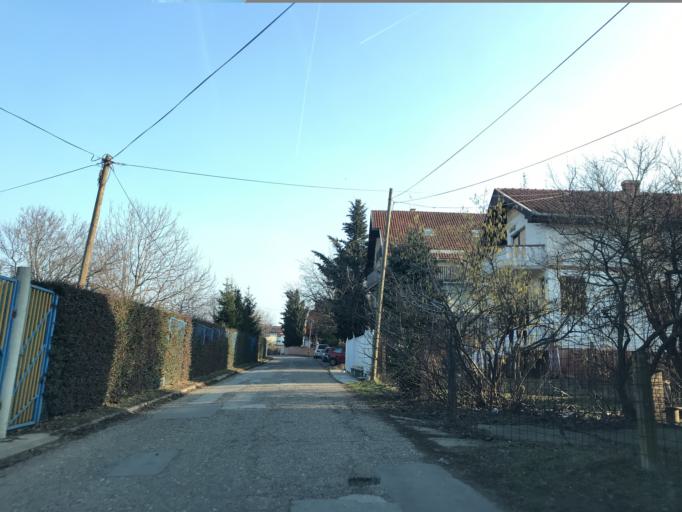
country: RS
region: Autonomna Pokrajina Vojvodina
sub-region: Juznobacki Okrug
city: Novi Sad
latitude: 45.2267
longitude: 19.8538
